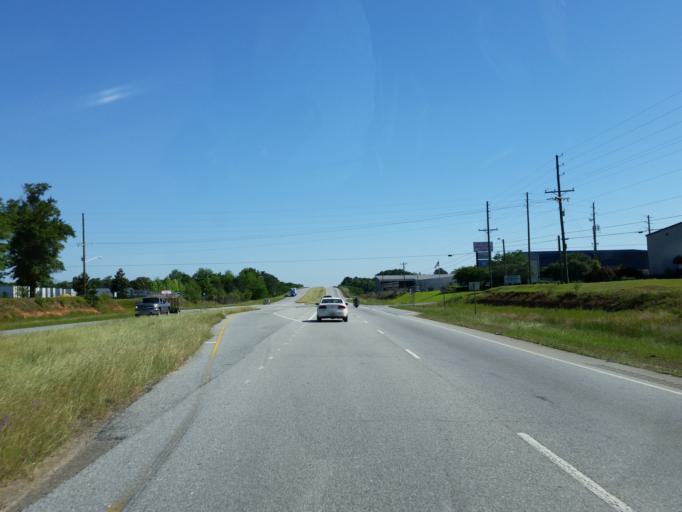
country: US
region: Georgia
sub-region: Lowndes County
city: Valdosta
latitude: 30.8367
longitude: -83.2281
